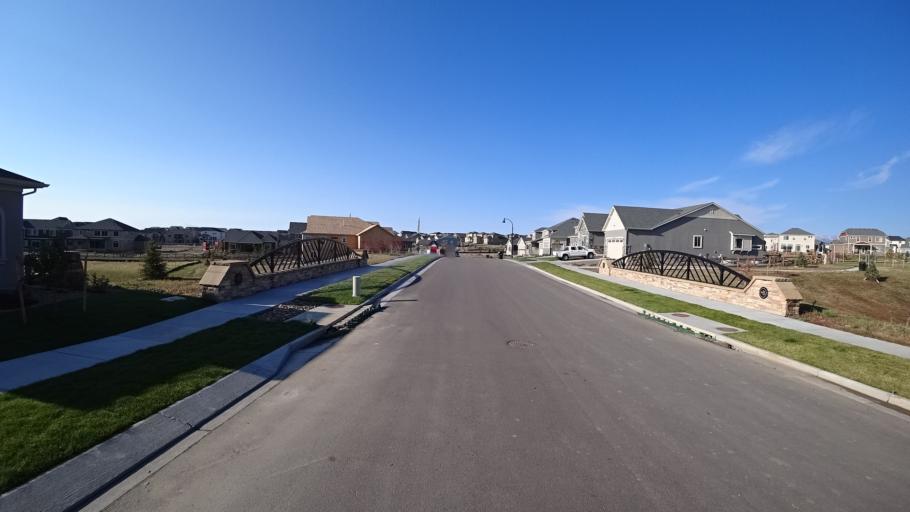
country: US
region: Colorado
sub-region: El Paso County
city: Cimarron Hills
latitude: 38.9332
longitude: -104.6542
